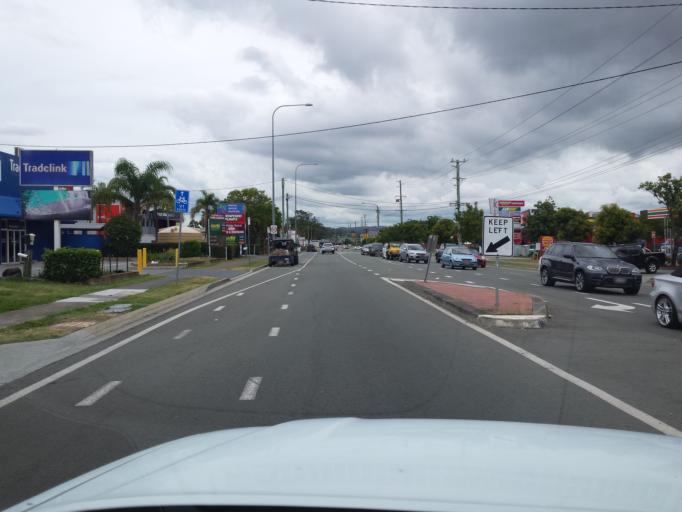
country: AU
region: Queensland
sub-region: Gold Coast
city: Oxenford
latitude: -27.8857
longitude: 153.3141
